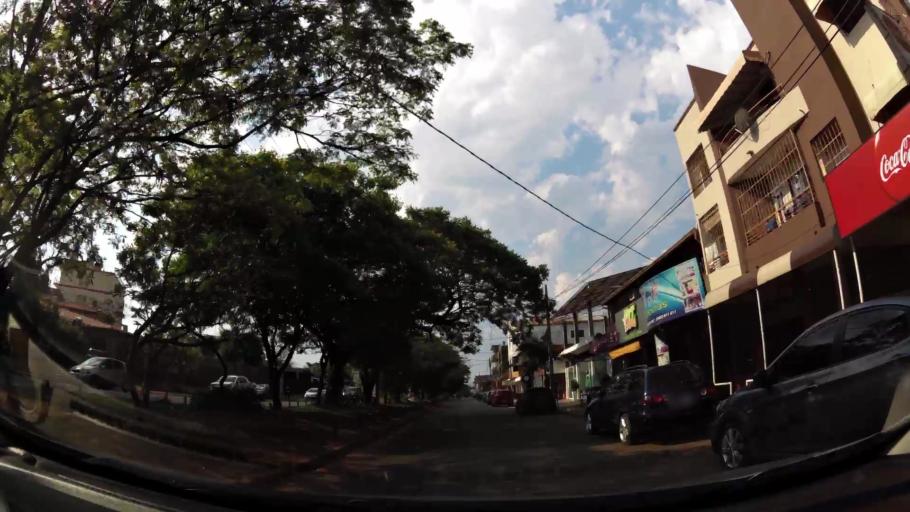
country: PY
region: Alto Parana
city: Presidente Franco
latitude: -25.5346
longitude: -54.6239
